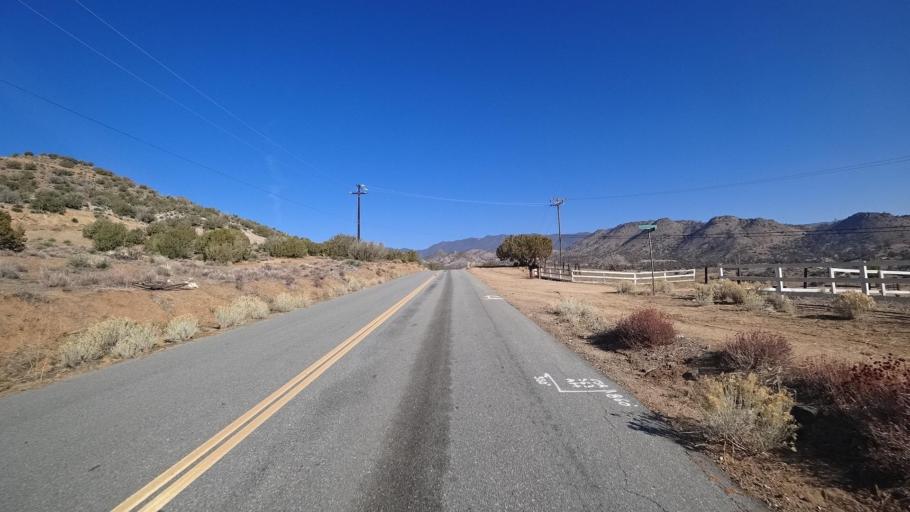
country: US
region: California
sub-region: Kern County
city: Tehachapi
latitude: 35.3482
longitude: -118.3859
